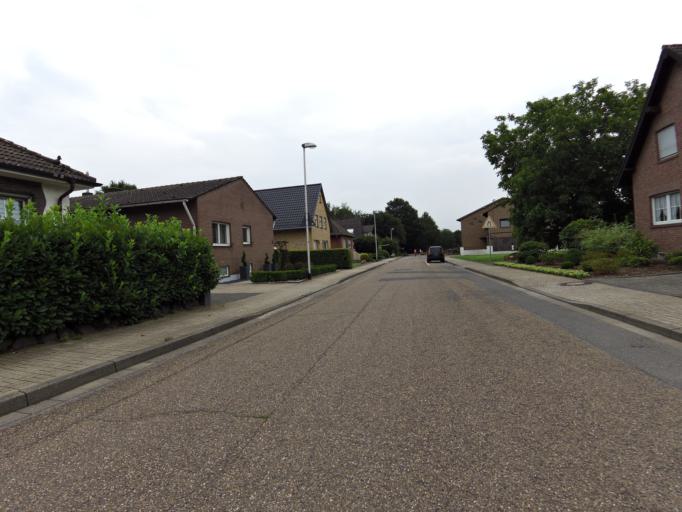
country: DE
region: North Rhine-Westphalia
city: Geilenkirchen
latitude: 50.9928
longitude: 6.1619
